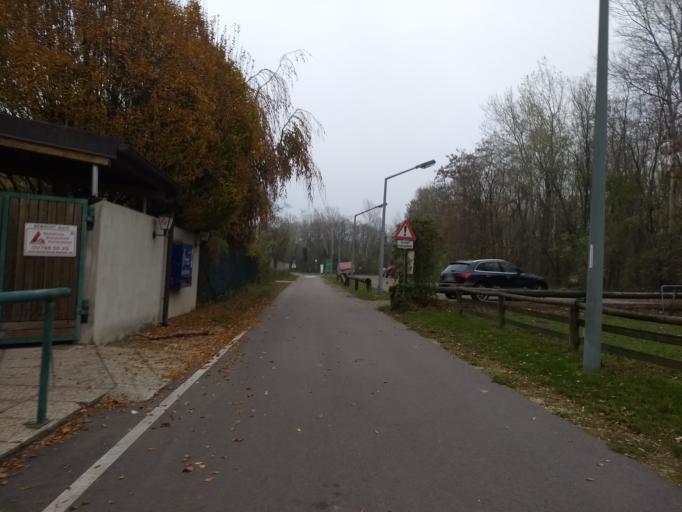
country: AT
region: Lower Austria
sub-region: Politischer Bezirk Tulln
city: Wordern
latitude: 48.3473
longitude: 16.2106
